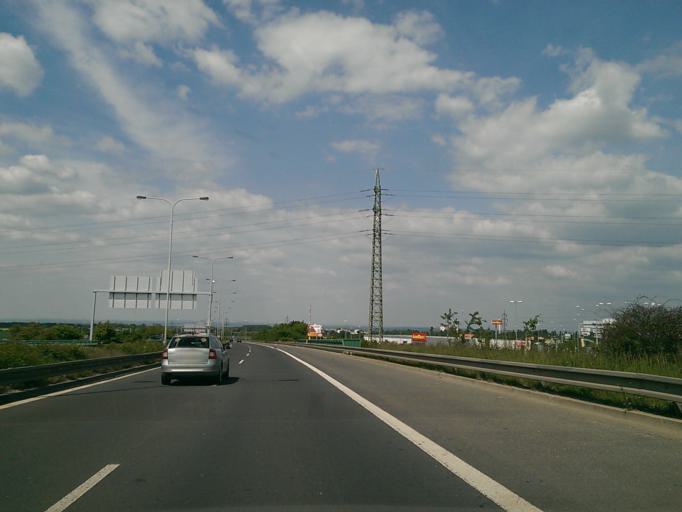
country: CZ
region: Praha
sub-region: Praha 9
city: Strizkov
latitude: 50.1348
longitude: 14.4923
